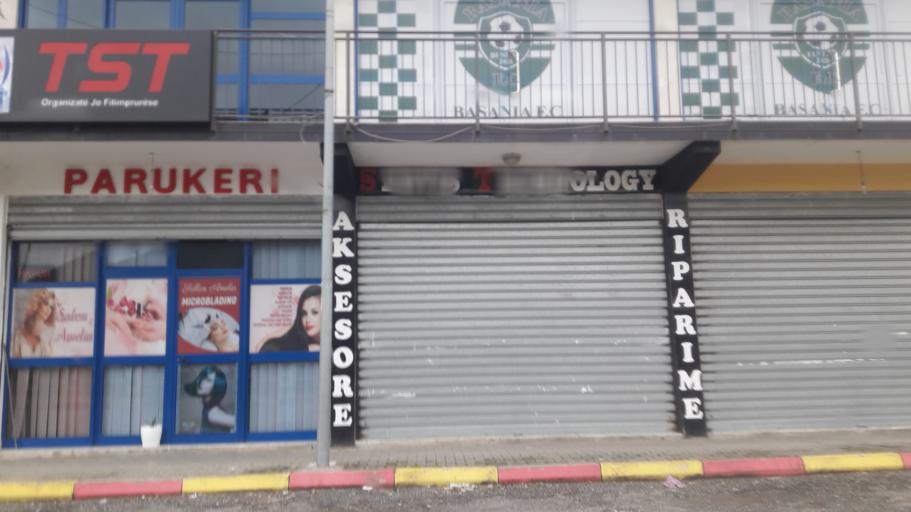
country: AL
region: Shkoder
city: Vukatane
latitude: 41.9597
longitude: 19.5353
